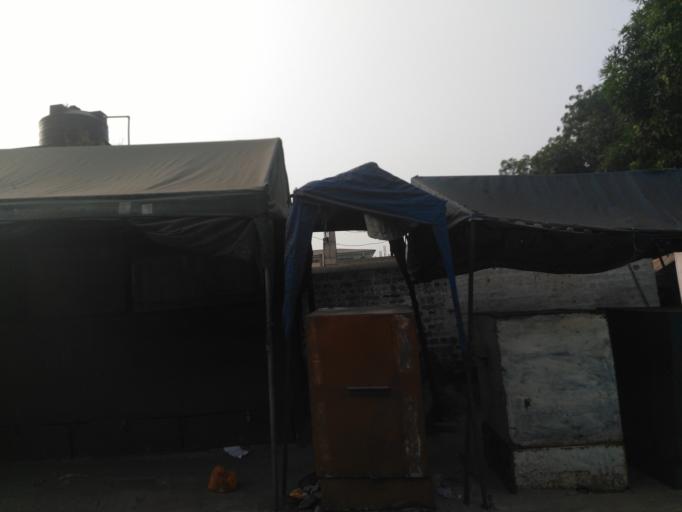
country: GH
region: Ashanti
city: Kumasi
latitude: 6.6906
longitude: -1.6100
